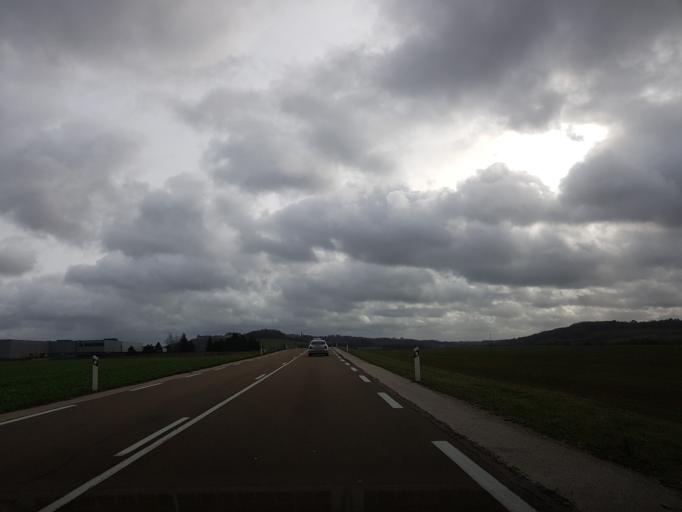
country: FR
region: Champagne-Ardenne
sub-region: Departement de la Haute-Marne
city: Langres
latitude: 47.8919
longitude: 5.3147
